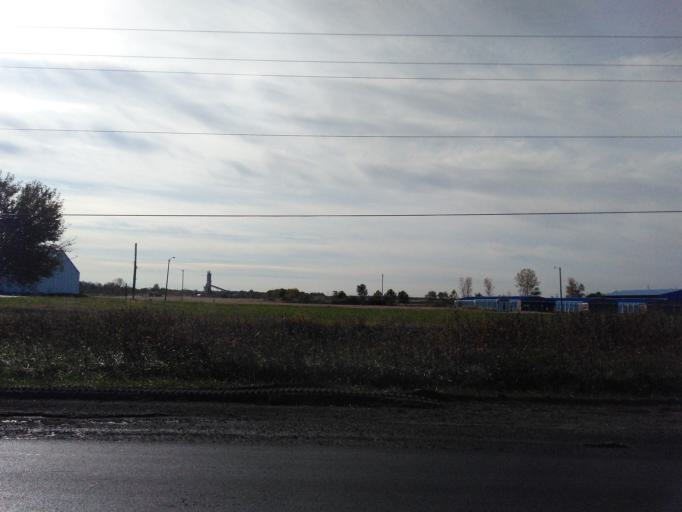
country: US
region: Illinois
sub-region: Madison County
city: Troy
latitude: 38.7175
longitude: -89.9071
